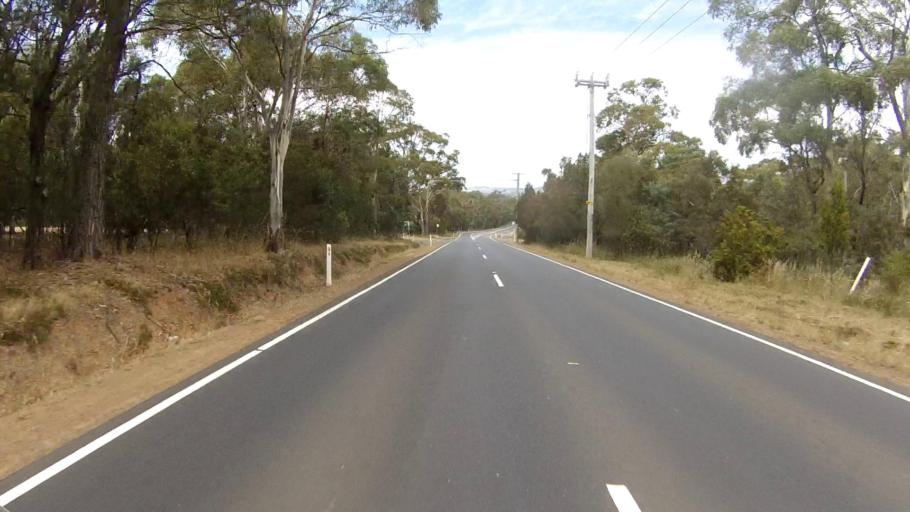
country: AU
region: Tasmania
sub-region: Clarence
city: Acton Park
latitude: -42.8830
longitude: 147.4826
